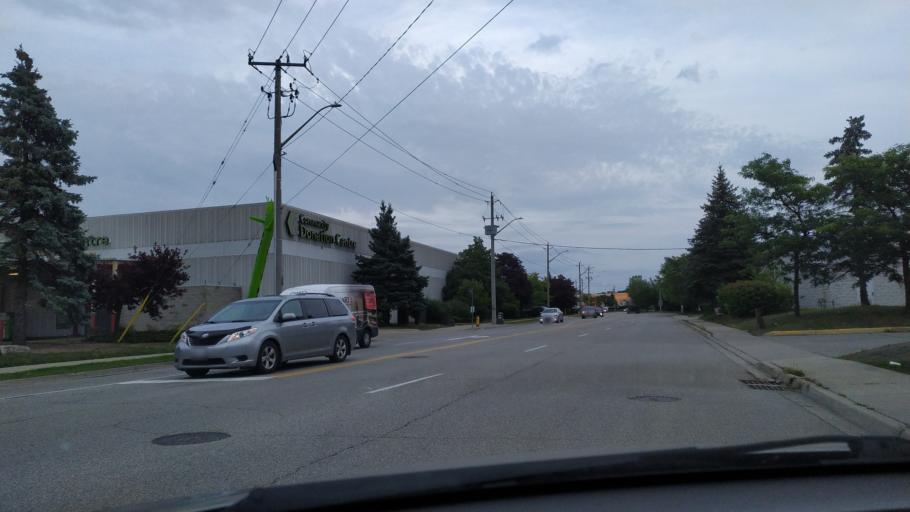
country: CA
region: Ontario
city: Cambridge
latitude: 43.4081
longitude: -80.3931
